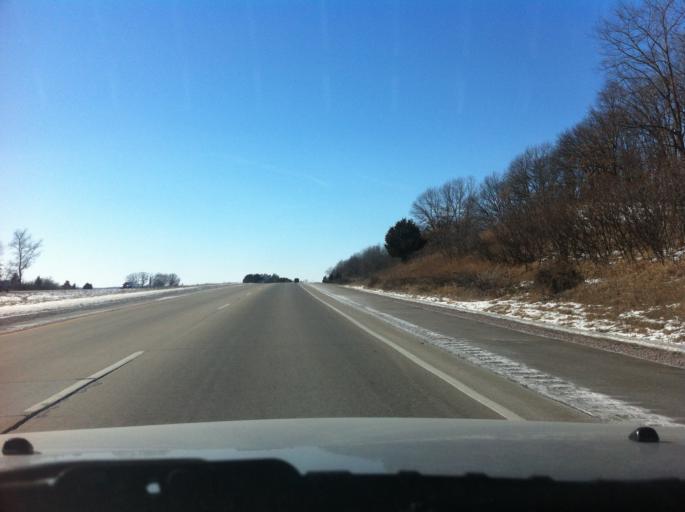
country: US
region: Wisconsin
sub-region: Sauk County
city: Baraboo
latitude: 43.5420
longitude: -89.6133
